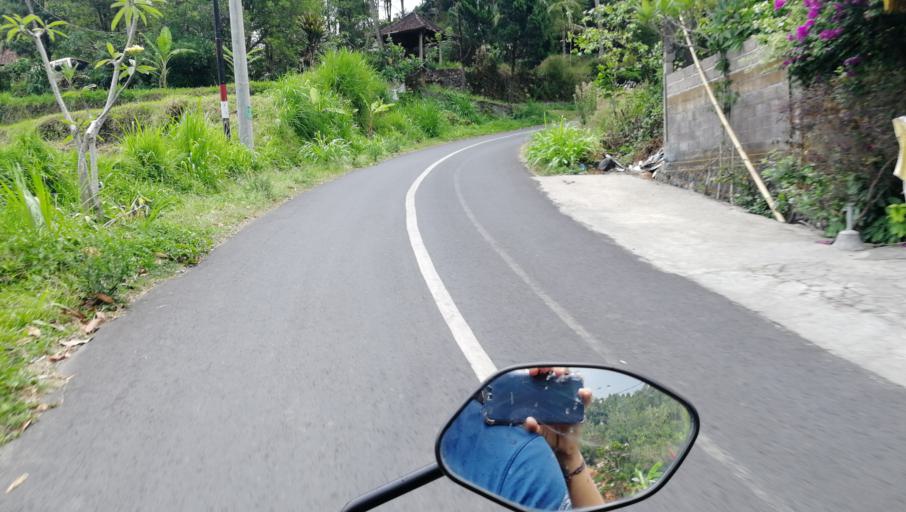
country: ID
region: Bali
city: Banjar Pedawa
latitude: -8.2649
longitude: 115.0287
